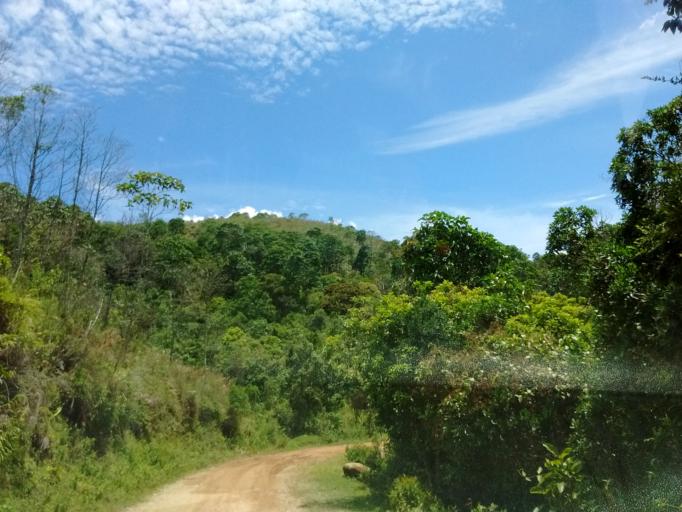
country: CO
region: Cauca
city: Villa Rica
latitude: 2.6008
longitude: -76.7576
